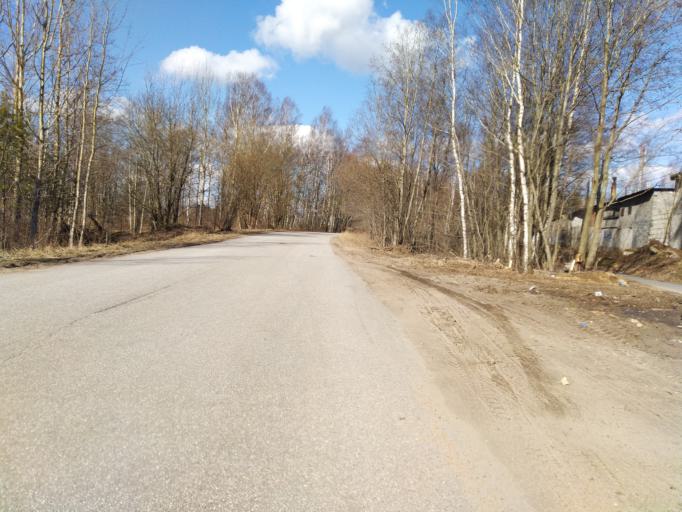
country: RU
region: Leningrad
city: Novoye Devyatkino
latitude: 60.1056
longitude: 30.4814
